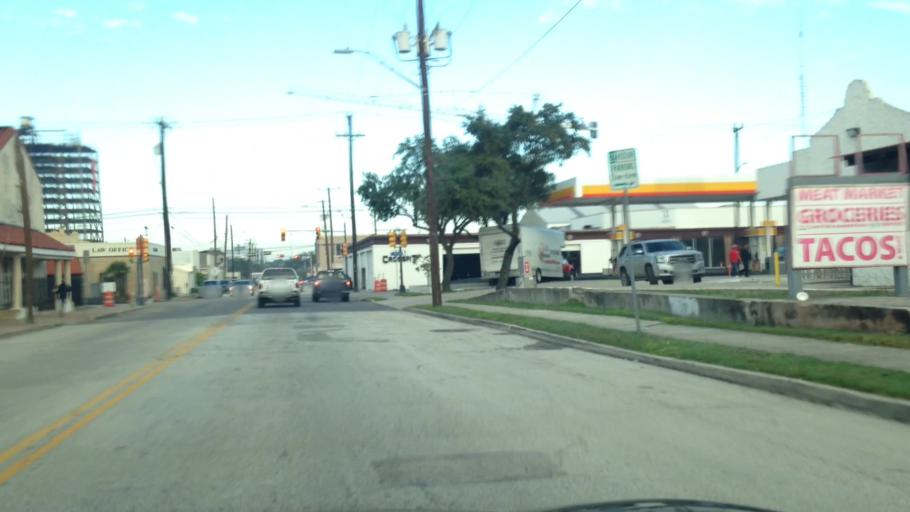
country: US
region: Texas
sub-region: Bexar County
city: San Antonio
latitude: 29.4307
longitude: -98.4821
